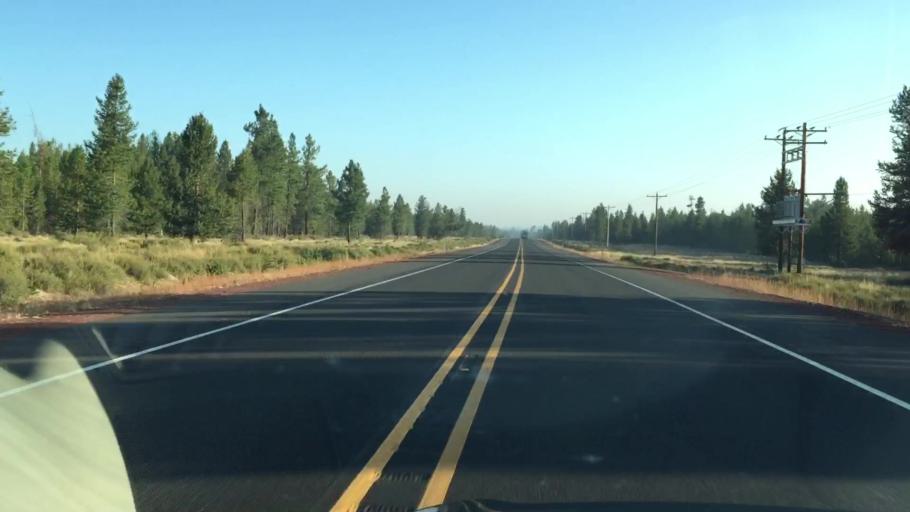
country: US
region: Oregon
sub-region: Deschutes County
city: La Pine
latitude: 43.1875
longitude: -121.7811
